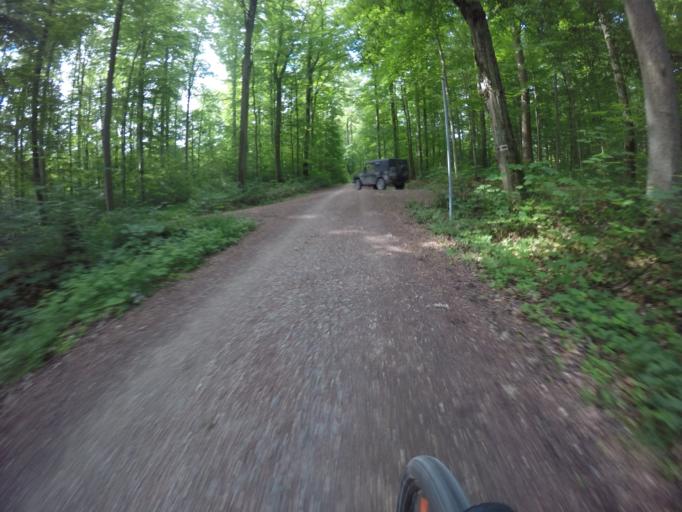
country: DE
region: Baden-Wuerttemberg
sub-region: Regierungsbezirk Stuttgart
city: Denkendorf
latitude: 48.6781
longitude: 9.3190
